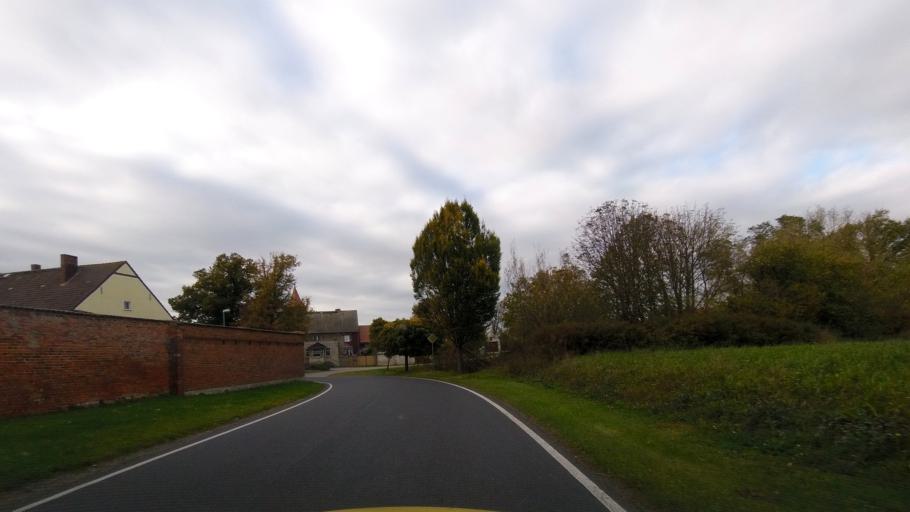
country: DE
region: Saxony-Anhalt
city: Zahna
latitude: 51.9778
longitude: 12.8316
